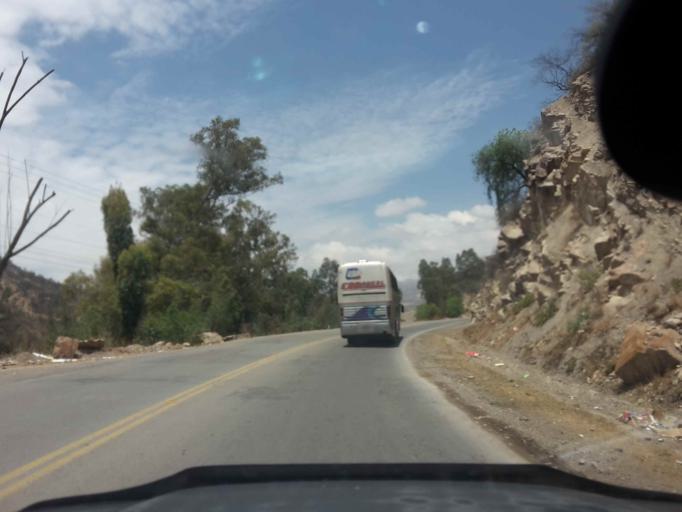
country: BO
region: Cochabamba
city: Sipe Sipe
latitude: -17.5389
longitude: -66.3355
